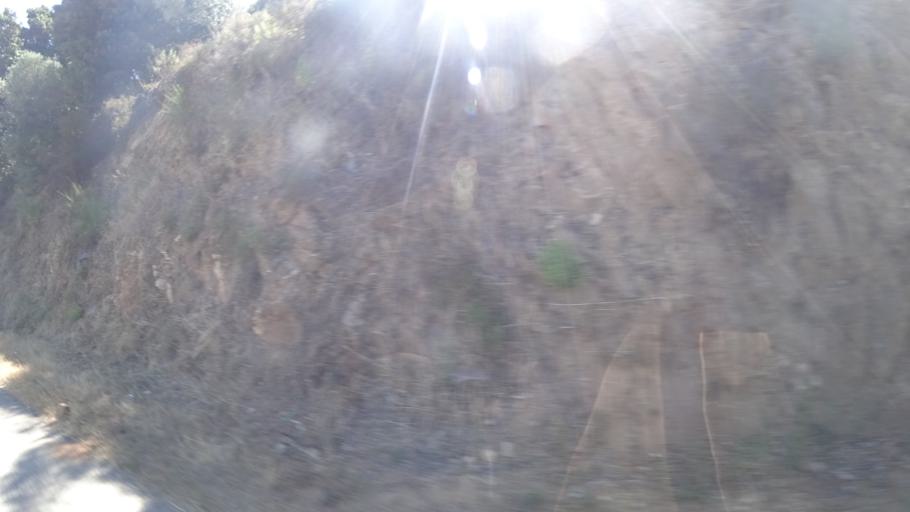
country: FR
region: Corsica
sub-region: Departement de la Corse-du-Sud
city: Alata
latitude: 41.9688
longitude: 8.7079
